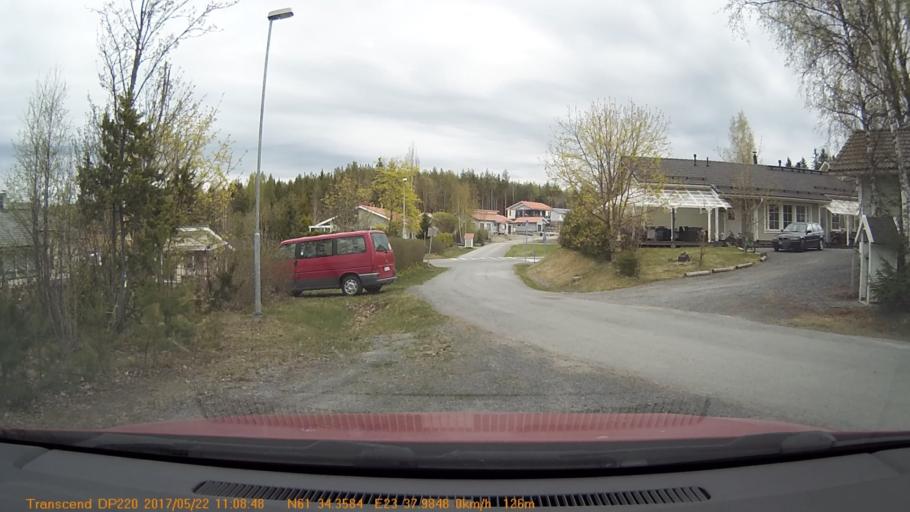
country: FI
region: Pirkanmaa
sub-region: Tampere
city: Yloejaervi
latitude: 61.5726
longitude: 23.6330
